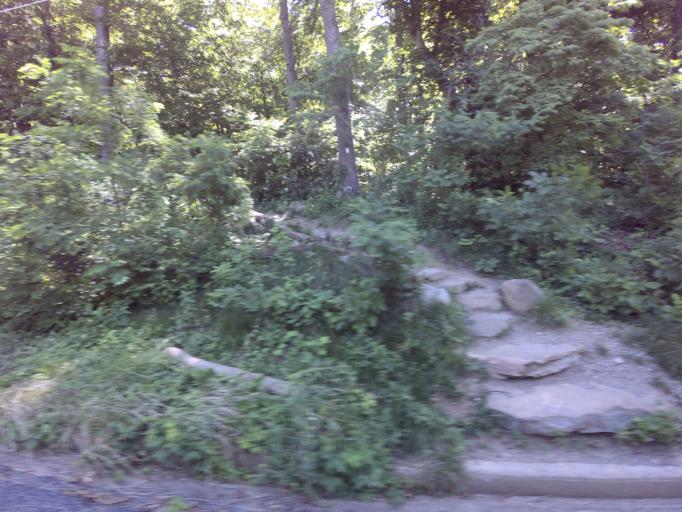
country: US
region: Maryland
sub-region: Frederick County
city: Brunswick
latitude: 39.3327
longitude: -77.6821
